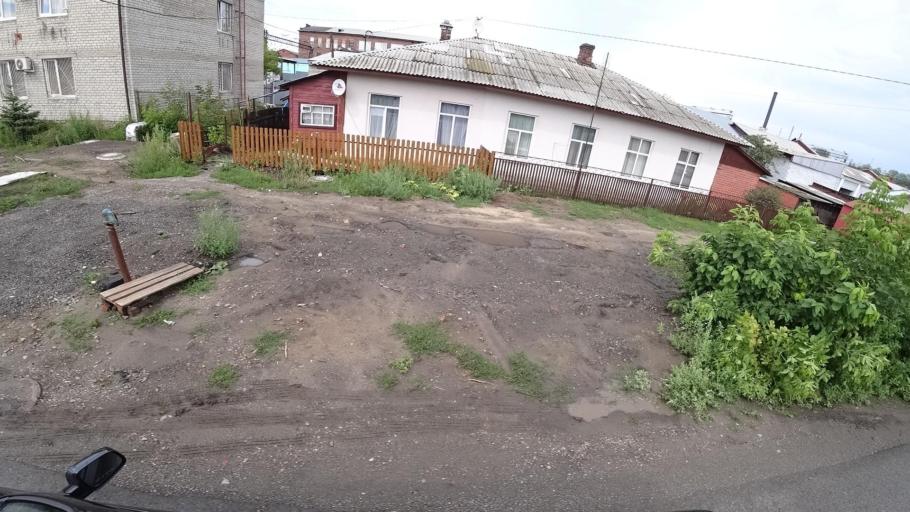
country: RU
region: Sverdlovsk
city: Kamyshlov
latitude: 56.8476
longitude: 62.7150
